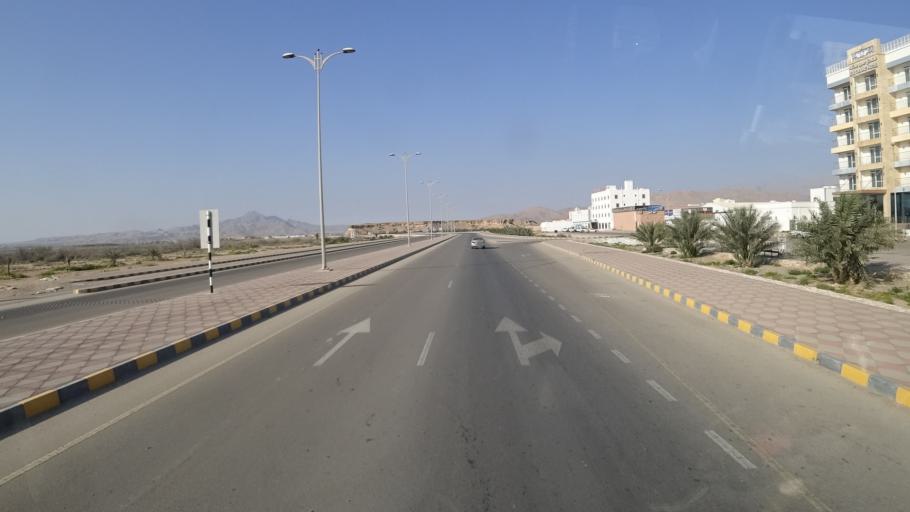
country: OM
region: Ash Sharqiyah
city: Sur
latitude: 22.6011
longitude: 59.4821
